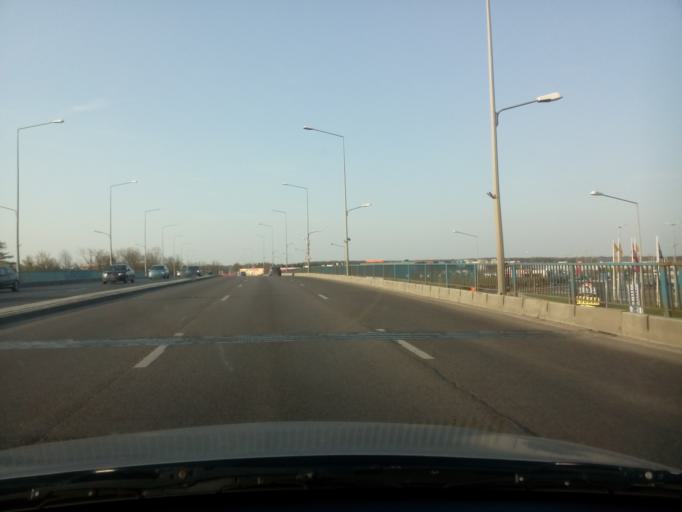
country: RO
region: Ilfov
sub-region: Comuna Otopeni
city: Otopeni
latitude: 44.5049
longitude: 26.0815
